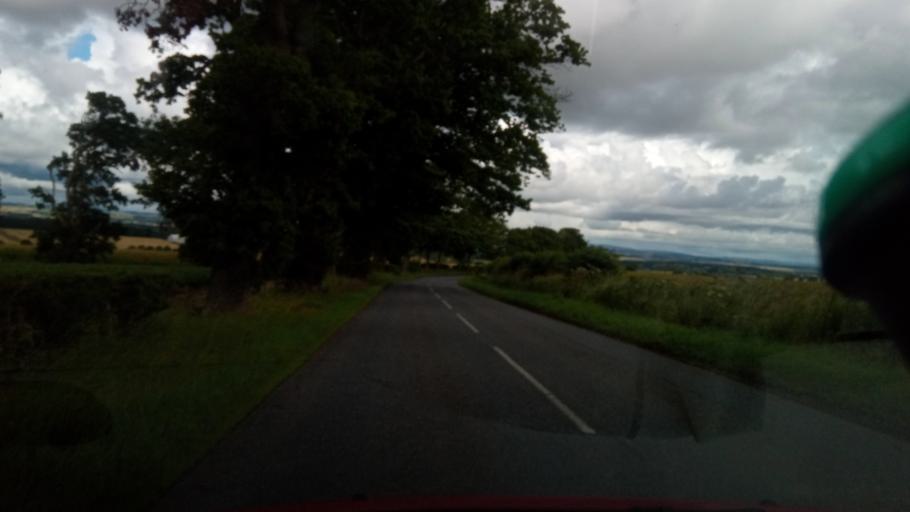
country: GB
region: Scotland
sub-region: The Scottish Borders
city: Kelso
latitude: 55.5709
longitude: -2.4199
